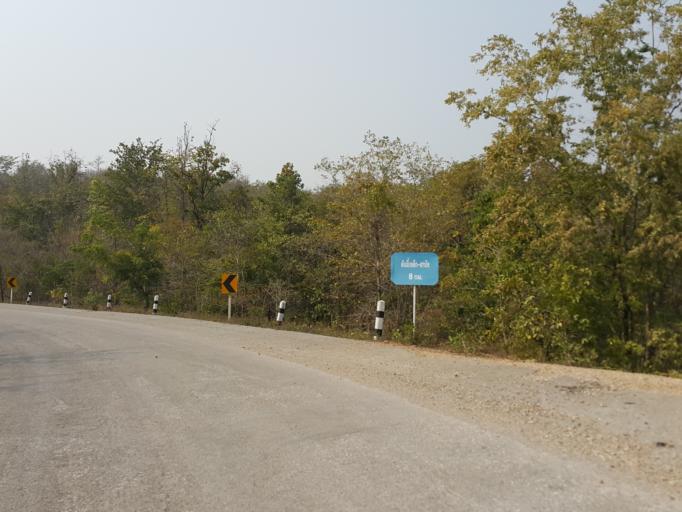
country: TH
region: Lampang
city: Mae Phrik
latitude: 17.5039
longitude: 99.0826
